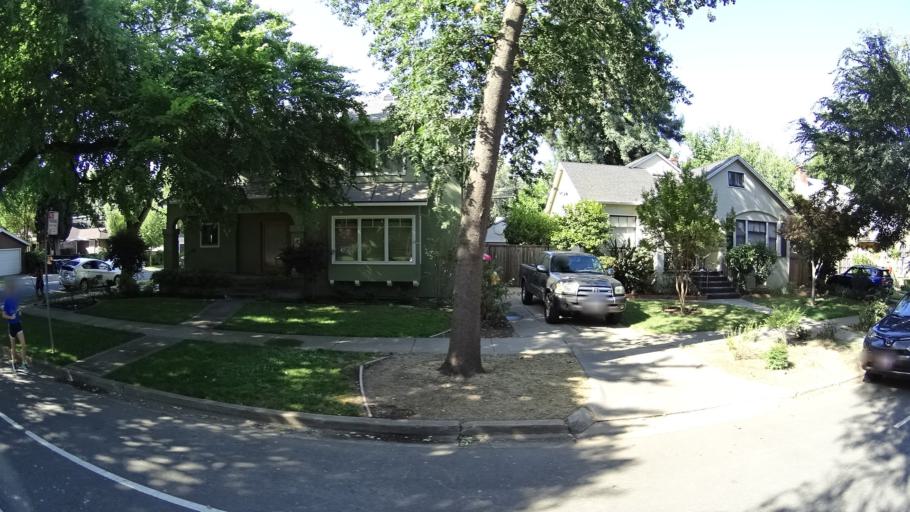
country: US
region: California
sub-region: Sacramento County
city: Sacramento
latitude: 38.5577
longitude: -121.4560
